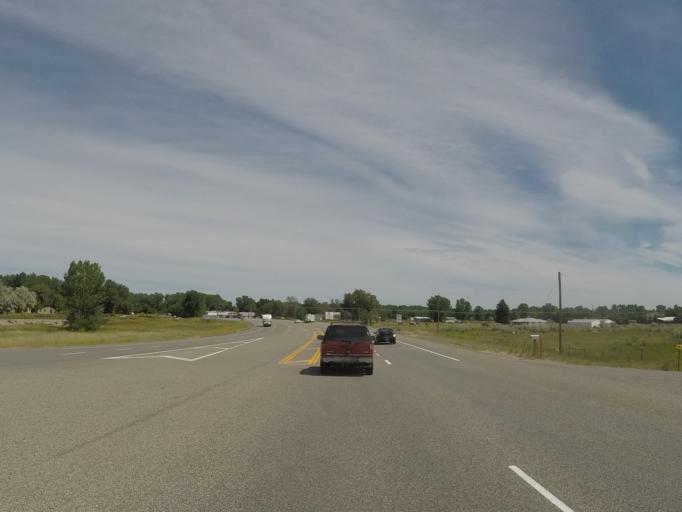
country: US
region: Montana
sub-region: Yellowstone County
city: Laurel
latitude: 45.6461
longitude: -108.7571
